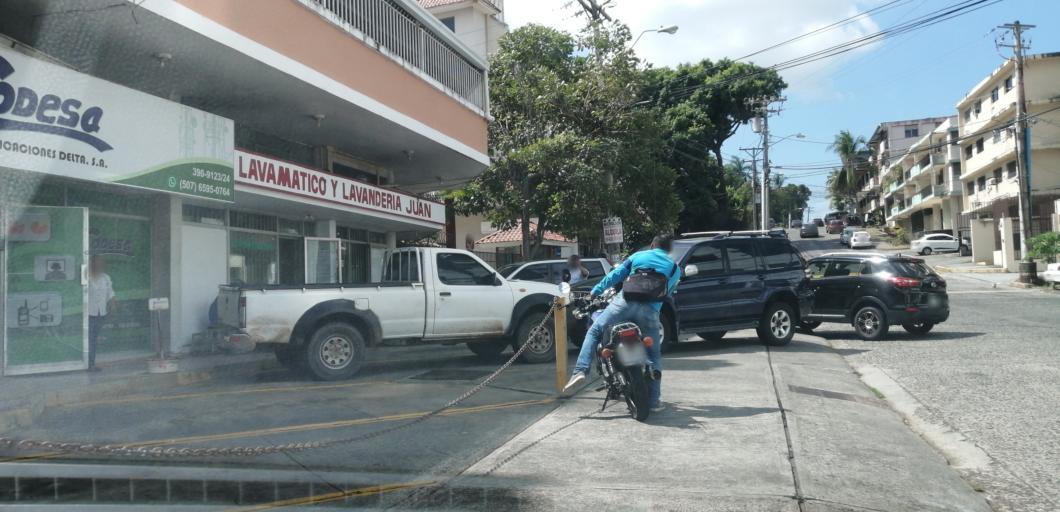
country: PA
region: Panama
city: Panama
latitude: 8.9775
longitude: -79.5361
